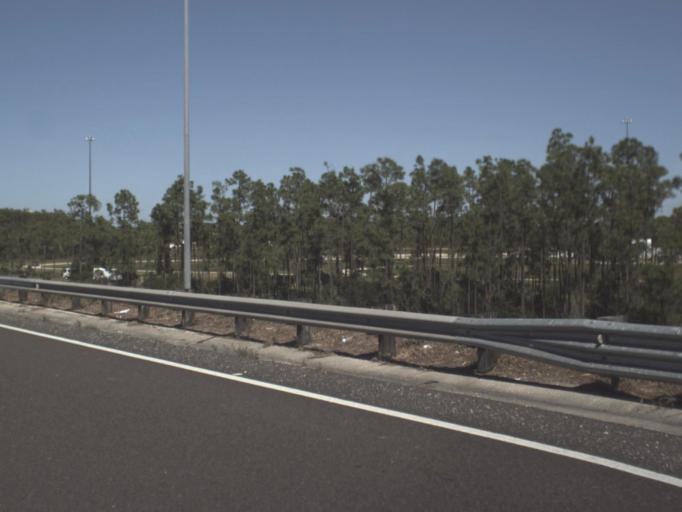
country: US
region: Florida
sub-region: Lee County
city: Gateway
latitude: 26.5477
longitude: -81.7948
